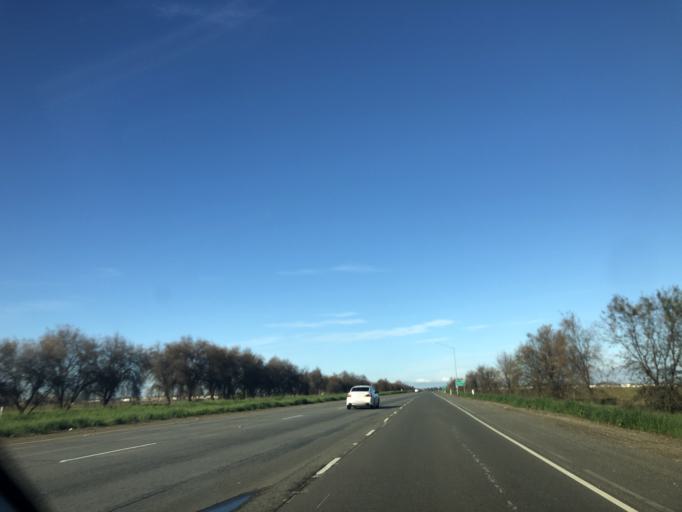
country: US
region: California
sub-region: Yolo County
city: Woodland
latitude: 38.6446
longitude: -121.7581
